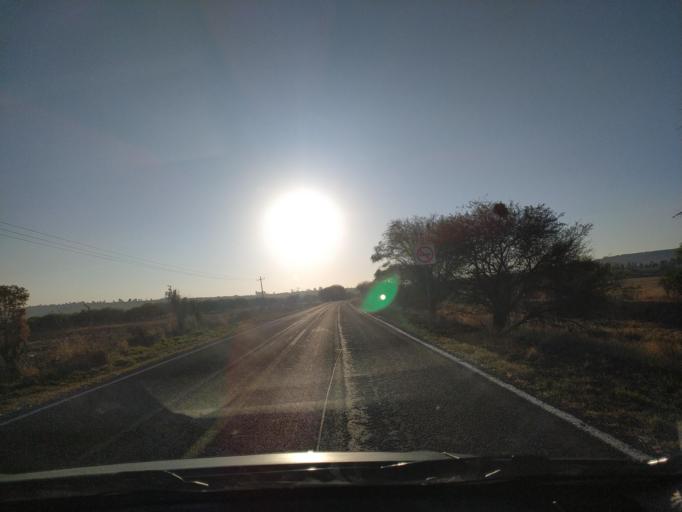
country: MX
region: Guanajuato
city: Ciudad Manuel Doblado
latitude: 20.7350
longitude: -101.8379
